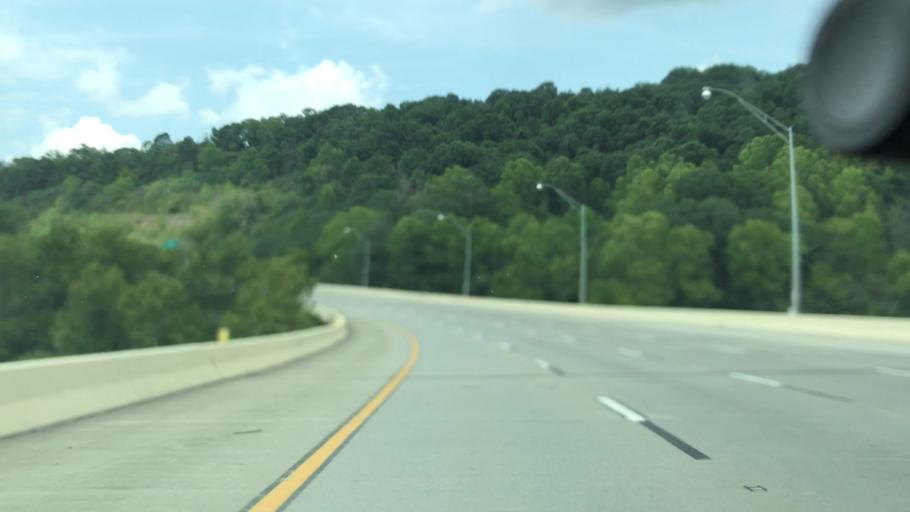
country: US
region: West Virginia
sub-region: Kanawha County
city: Dunbar
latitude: 38.3628
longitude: -81.7197
